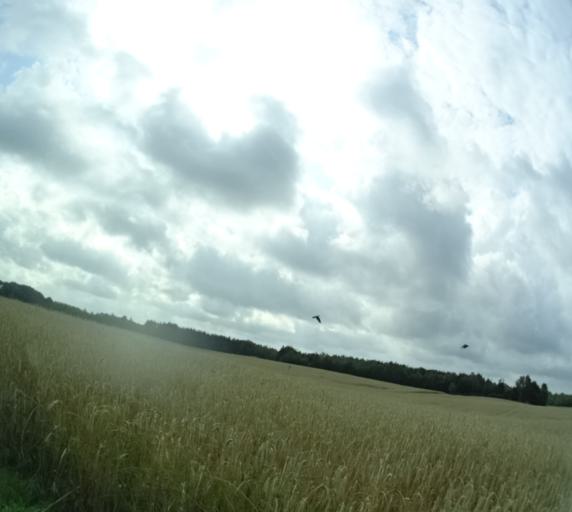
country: DK
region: Central Jutland
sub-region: Syddjurs Kommune
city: Ryomgard
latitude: 56.4010
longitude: 10.4981
